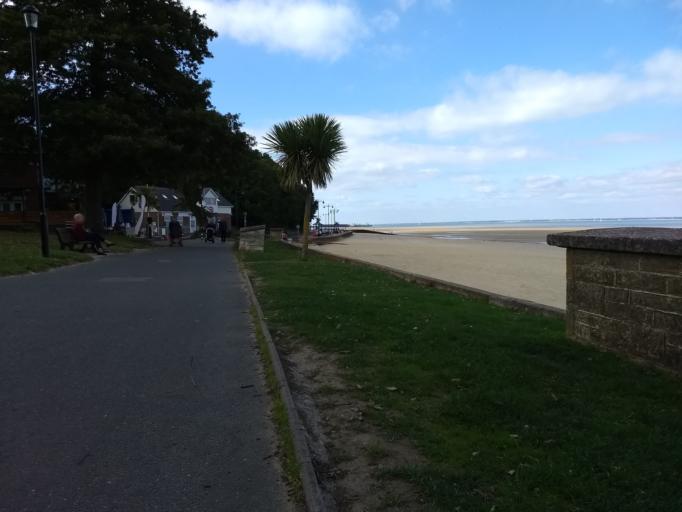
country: GB
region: England
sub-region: Isle of Wight
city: Ryde
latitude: 50.7281
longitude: -1.1426
